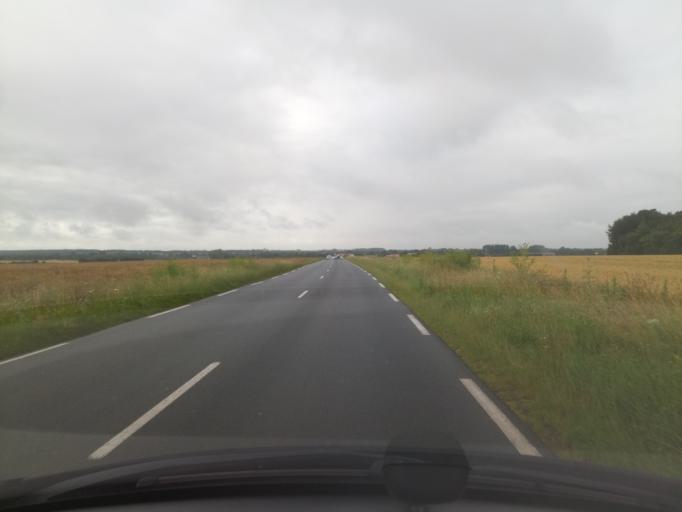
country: FR
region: Poitou-Charentes
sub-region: Departement de la Charente-Maritime
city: Saint-Jean-de-Liversay
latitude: 46.2004
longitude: -0.8718
